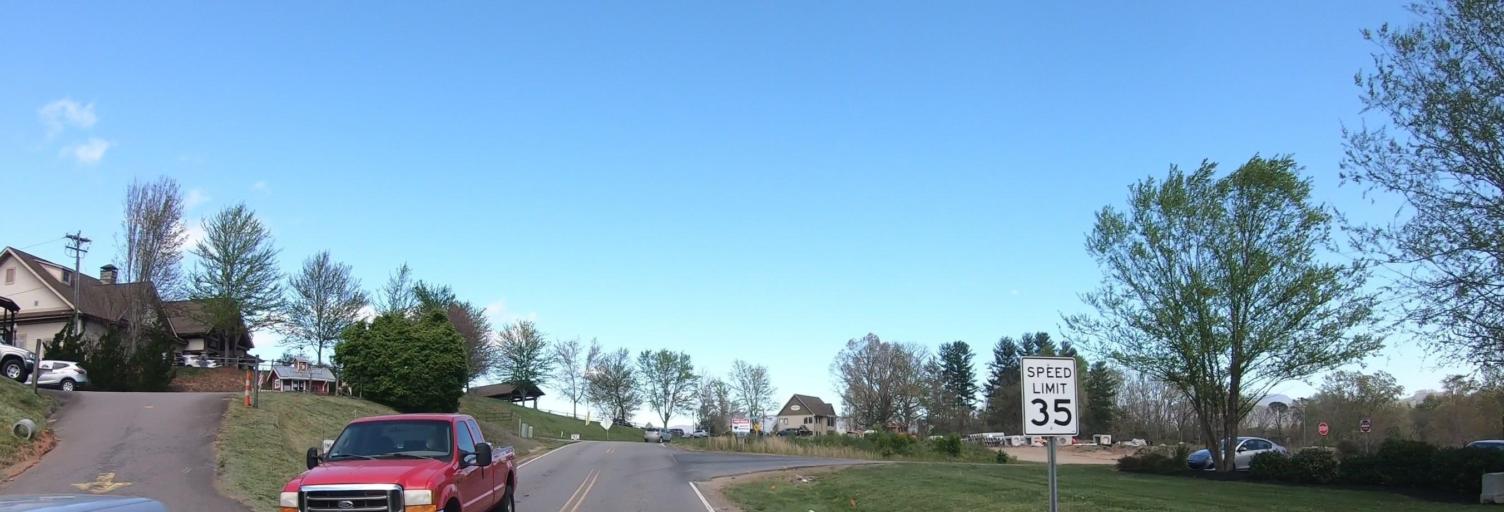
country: US
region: North Carolina
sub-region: Macon County
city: Franklin
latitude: 35.1639
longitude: -83.3908
